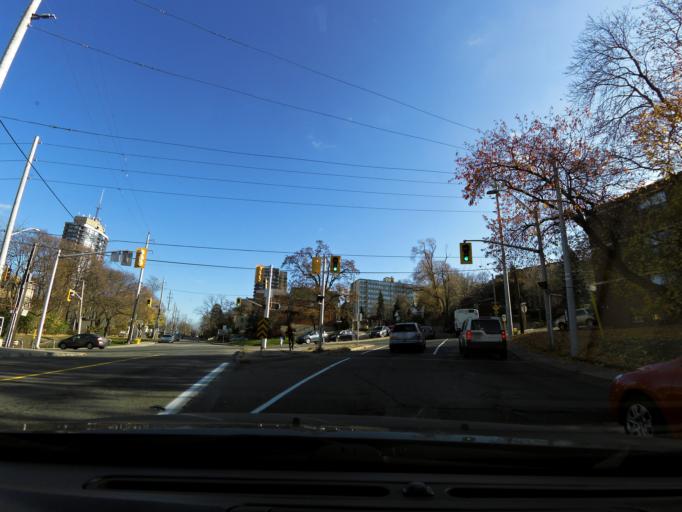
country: CA
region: Ontario
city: Hamilton
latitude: 43.2478
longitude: -79.8702
